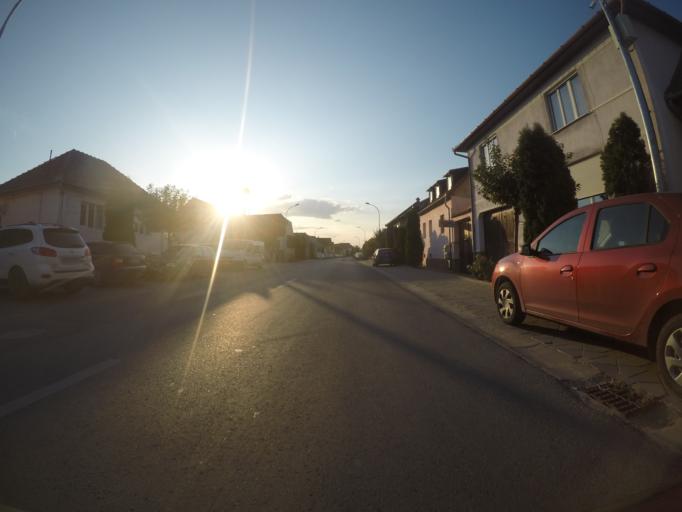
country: RO
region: Sibiu
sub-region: Comuna Selimbar
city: Selimbar
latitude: 45.7692
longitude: 24.1884
